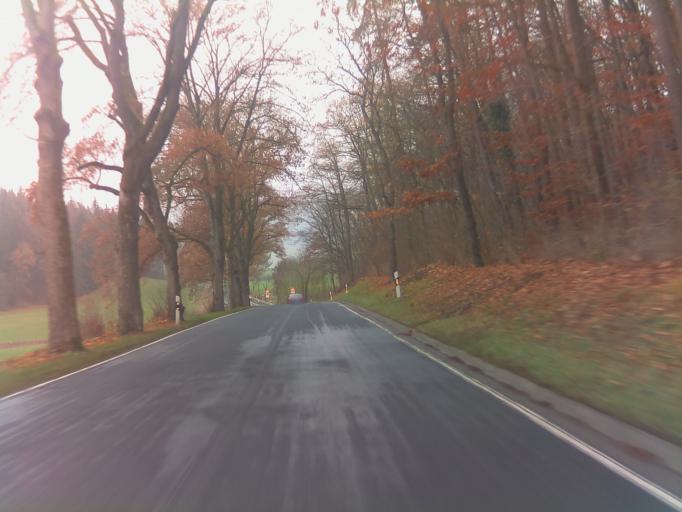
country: DE
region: Thuringia
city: Leutersdorf
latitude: 50.4738
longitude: 10.5478
